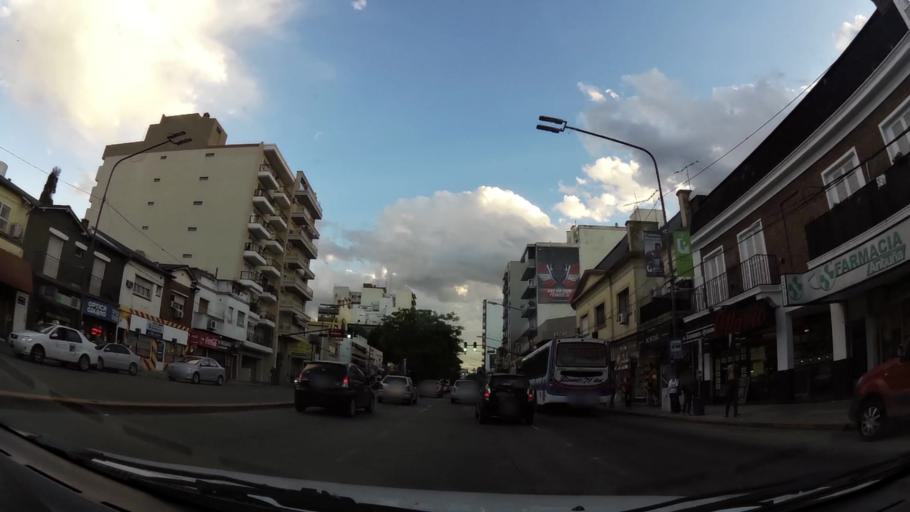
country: AR
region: Buenos Aires
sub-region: Partido de Vicente Lopez
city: Olivos
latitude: -34.5095
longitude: -58.4917
